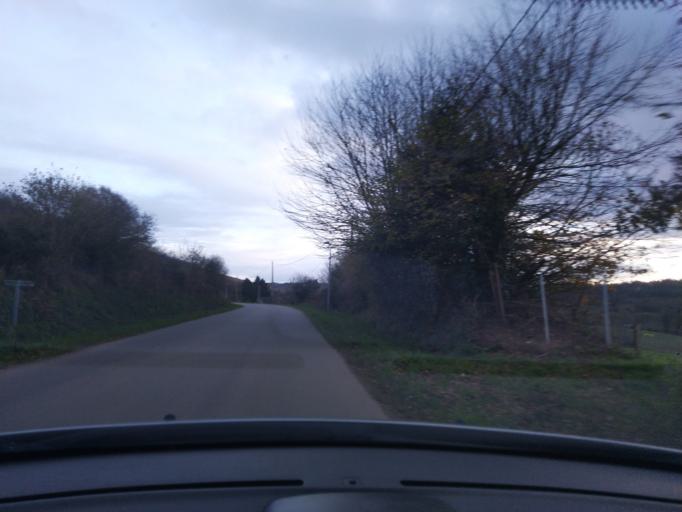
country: FR
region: Brittany
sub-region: Departement du Finistere
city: Guerlesquin
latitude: 48.5432
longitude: -3.6195
